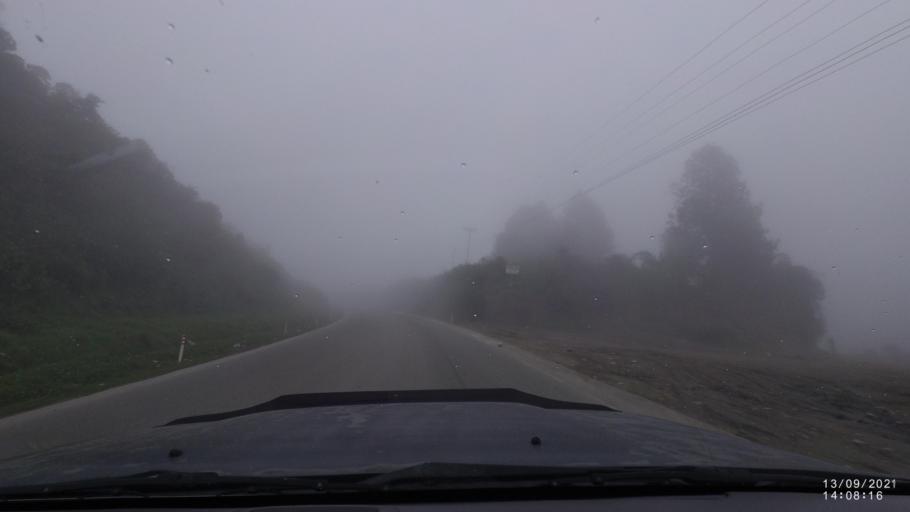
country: BO
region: Cochabamba
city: Colomi
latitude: -17.1718
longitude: -65.8893
